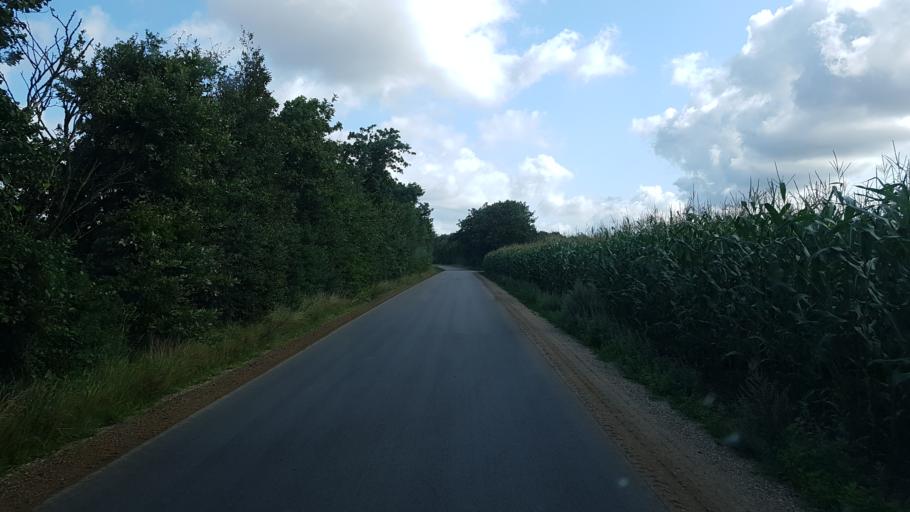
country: DK
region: South Denmark
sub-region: Varde Kommune
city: Olgod
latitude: 55.7815
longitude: 8.7213
